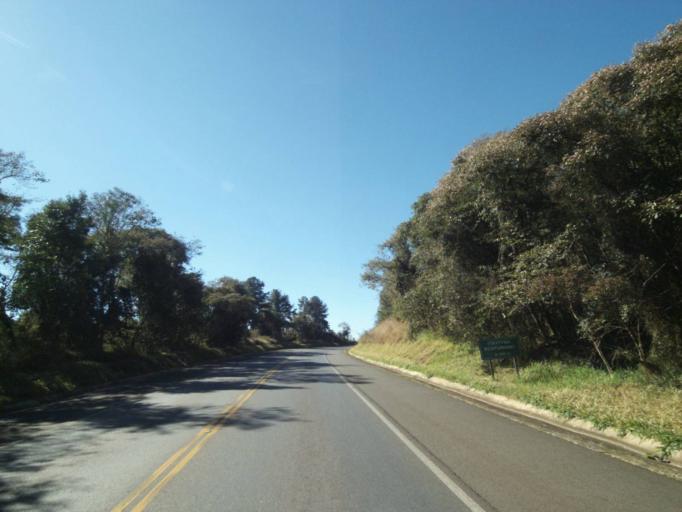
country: BR
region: Parana
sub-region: Tibagi
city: Tibagi
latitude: -24.4090
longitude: -50.3534
